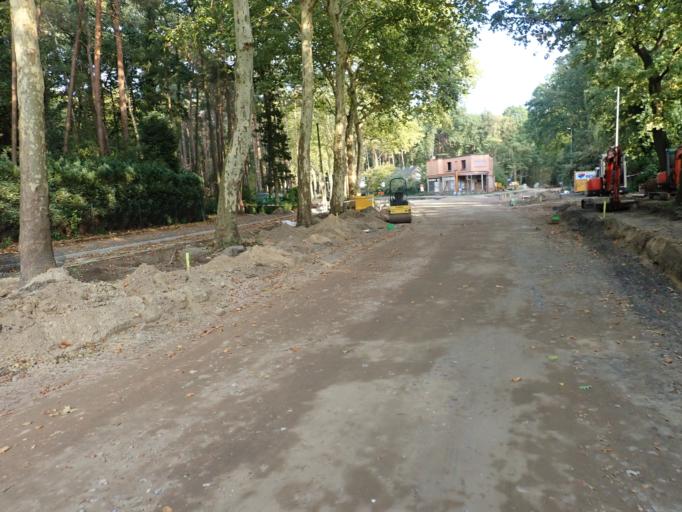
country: BE
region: Flanders
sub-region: Provincie Oost-Vlaanderen
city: Temse
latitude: 51.1748
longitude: 4.2012
